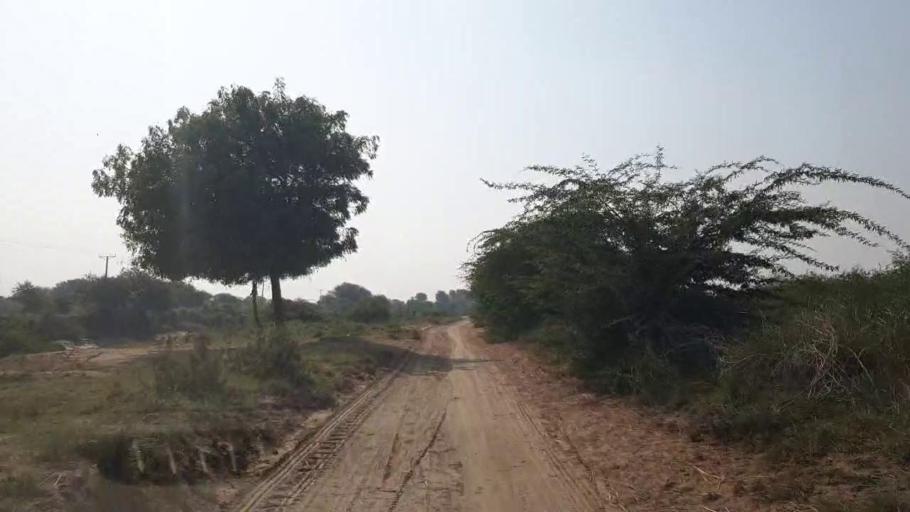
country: PK
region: Sindh
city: Matli
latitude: 24.9518
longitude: 68.6029
